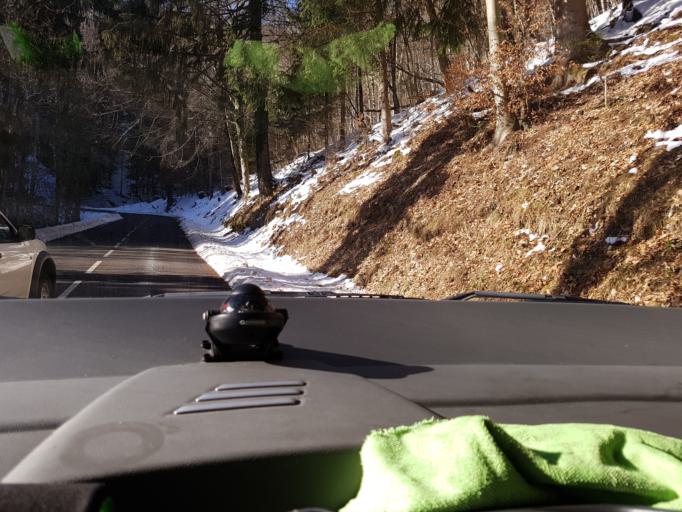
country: FR
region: Alsace
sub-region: Departement du Haut-Rhin
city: Metzeral
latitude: 47.9956
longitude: 7.0642
